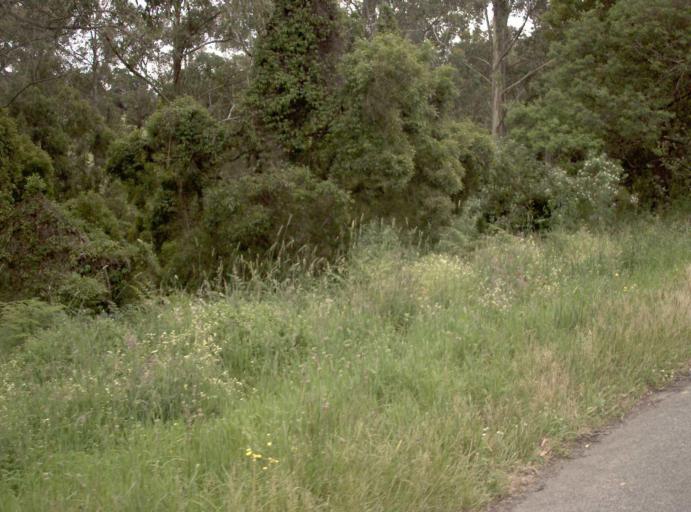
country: AU
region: Victoria
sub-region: Bass Coast
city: North Wonthaggi
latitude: -38.4481
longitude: 145.8471
